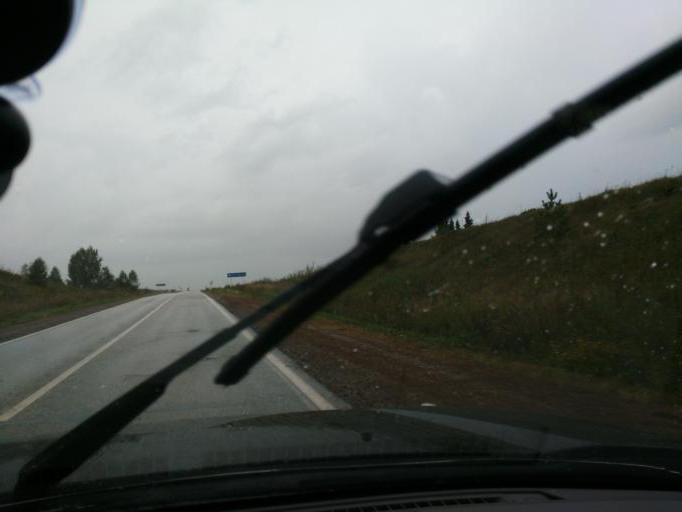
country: RU
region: Perm
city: Barda
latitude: 57.0922
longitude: 55.5358
